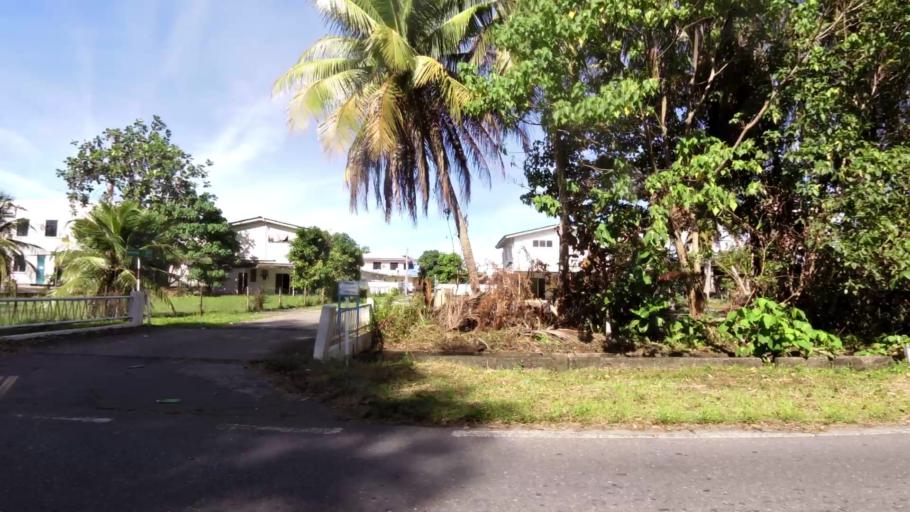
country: BN
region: Belait
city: Kuala Belait
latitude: 4.5789
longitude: 114.2083
